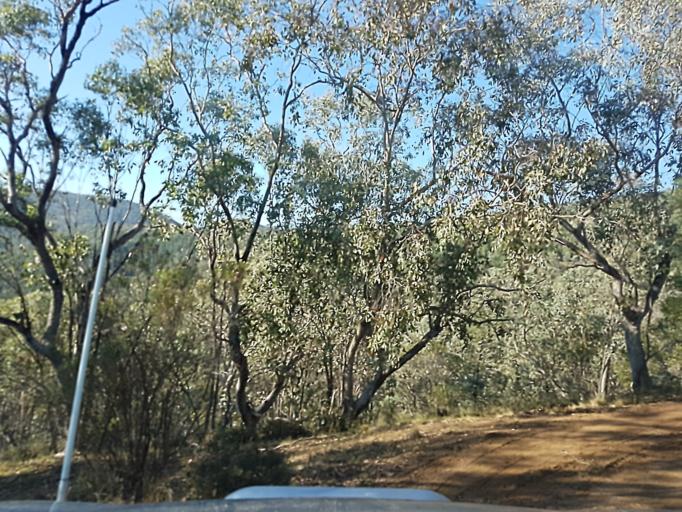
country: AU
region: New South Wales
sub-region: Snowy River
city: Jindabyne
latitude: -36.9563
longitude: 148.3834
